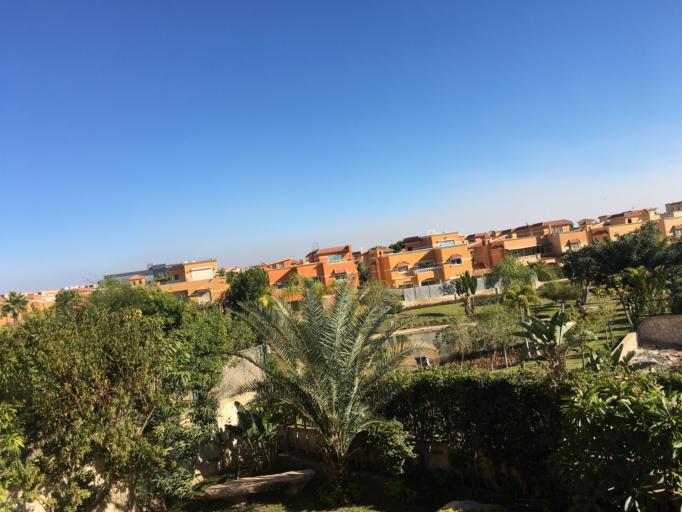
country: EG
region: Al Jizah
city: Awsim
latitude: 30.0653
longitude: 30.9500
